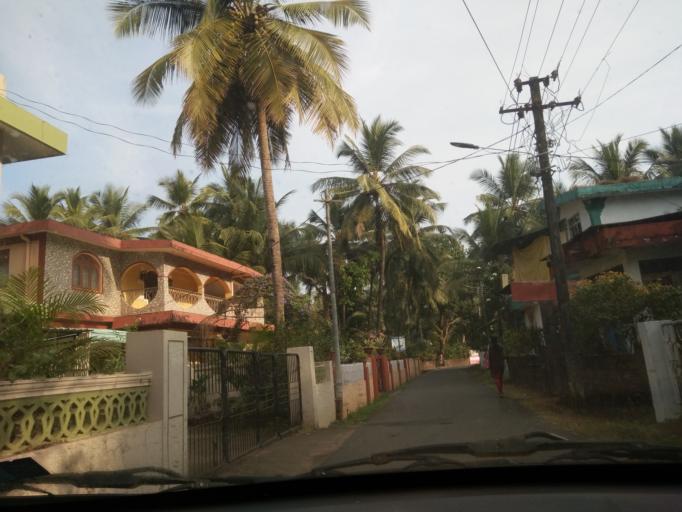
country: IN
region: Goa
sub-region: South Goa
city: Chinchinim
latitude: 15.2118
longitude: 73.9825
